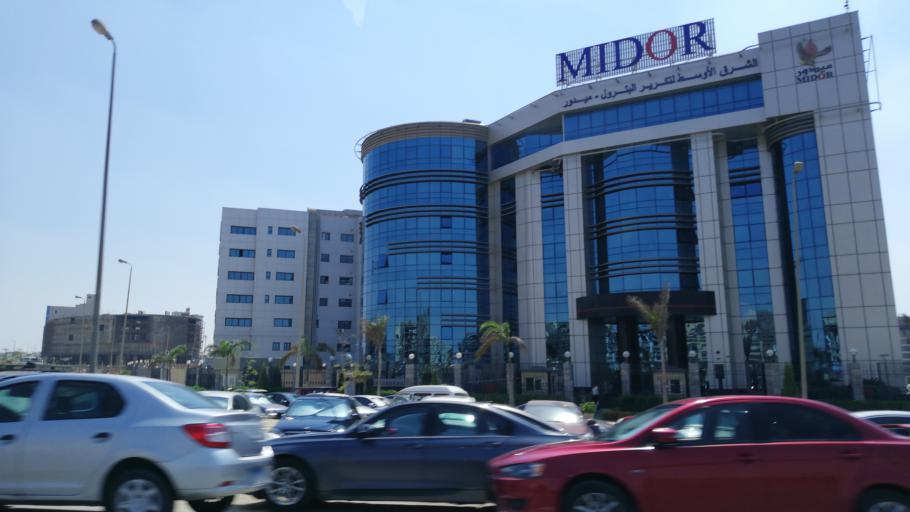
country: EG
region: Muhafazat al Qalyubiyah
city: Al Khankah
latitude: 30.0300
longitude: 31.4674
